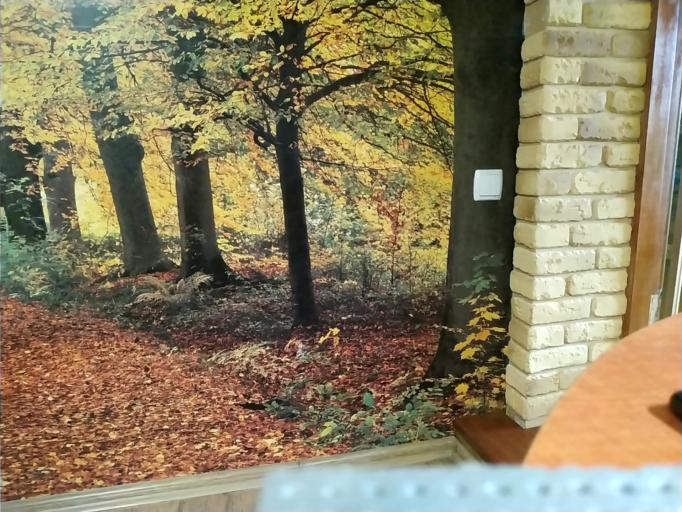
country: RU
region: Vladimir
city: Bavleny
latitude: 56.3689
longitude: 39.5852
